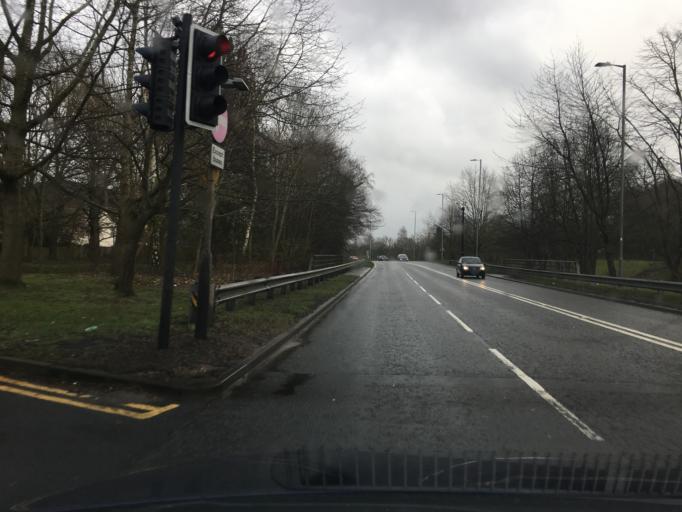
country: GB
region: England
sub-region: Bracknell Forest
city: Bracknell
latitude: 51.4098
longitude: -0.7532
